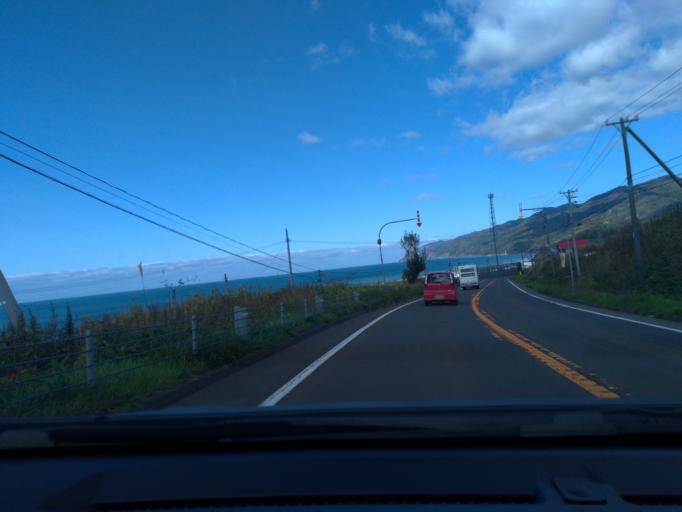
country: JP
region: Hokkaido
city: Ishikari
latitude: 43.3916
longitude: 141.4331
